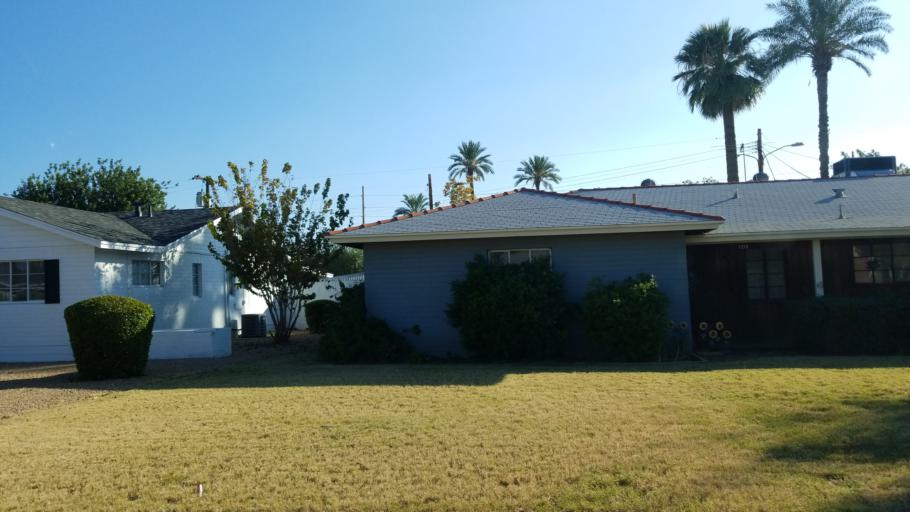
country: US
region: Arizona
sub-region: Maricopa County
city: Phoenix
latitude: 33.4774
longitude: -112.0556
